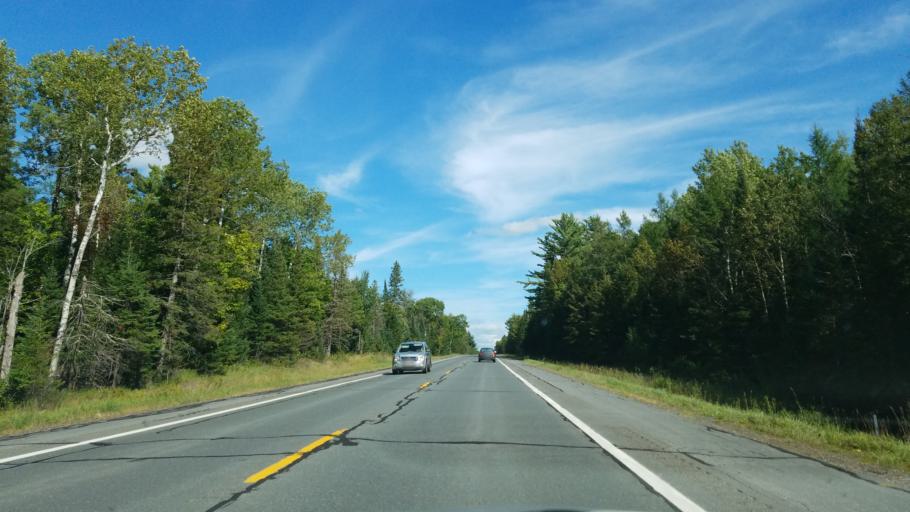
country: US
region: Michigan
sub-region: Baraga County
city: L'Anse
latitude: 46.5788
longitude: -88.4115
